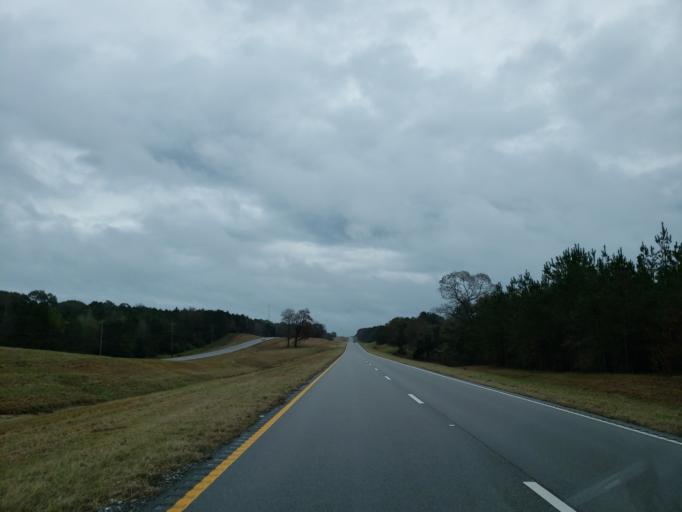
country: US
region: Mississippi
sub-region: Wayne County
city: Waynesboro
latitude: 31.6950
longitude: -88.7635
